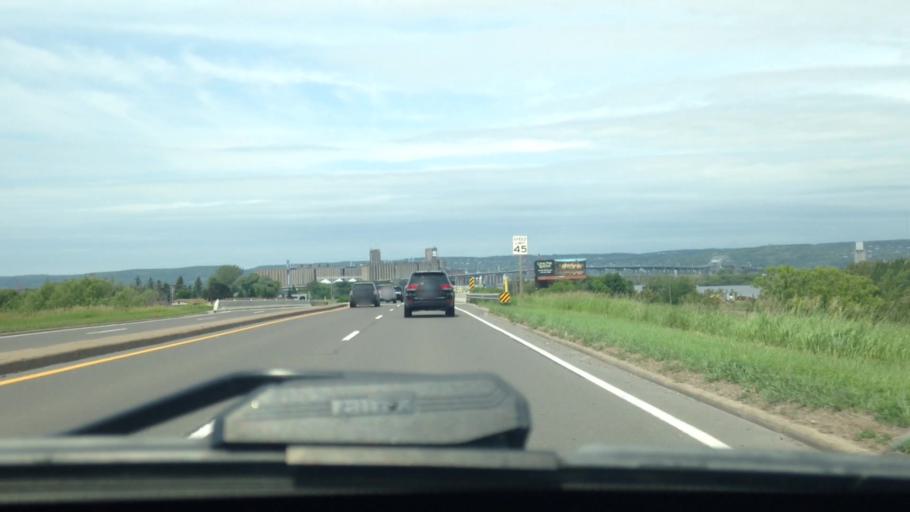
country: US
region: Wisconsin
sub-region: Douglas County
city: Superior
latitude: 46.7308
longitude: -92.0817
